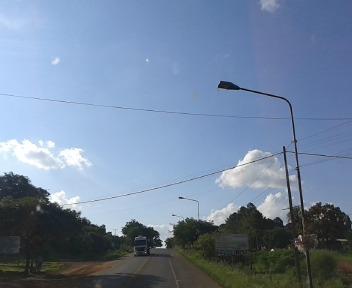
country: AR
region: Misiones
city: Guarani
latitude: -27.4943
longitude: -55.1693
